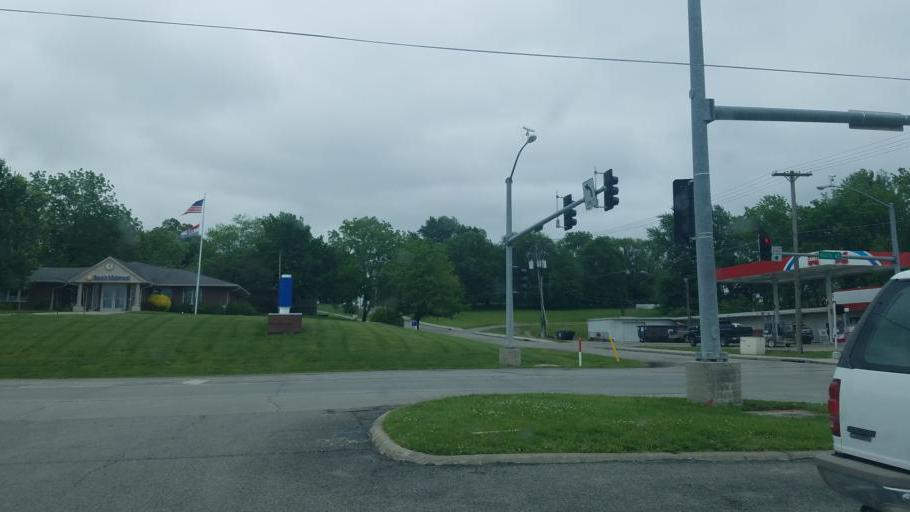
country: US
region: Missouri
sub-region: Carroll County
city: Carrollton
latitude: 39.3700
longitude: -93.4853
